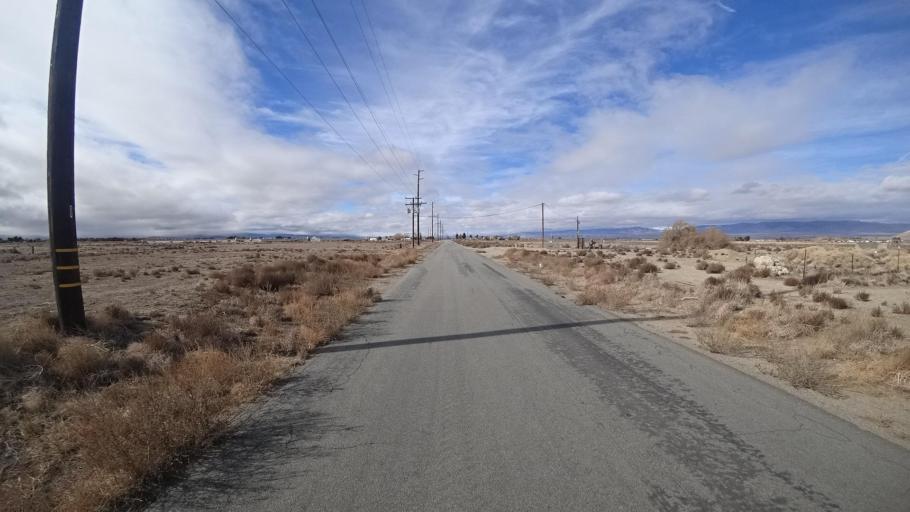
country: US
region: California
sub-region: Kern County
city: Rosamond
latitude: 34.8345
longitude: -118.2593
